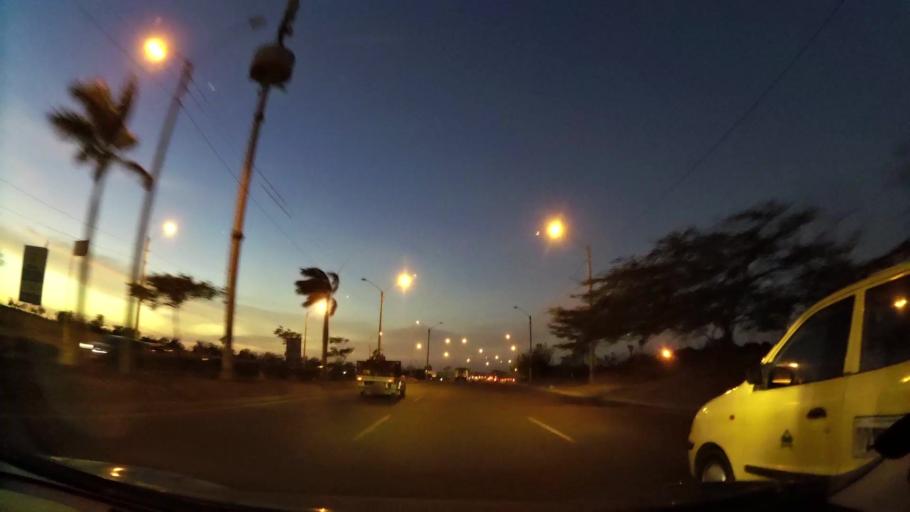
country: CO
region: Atlantico
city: Galapa
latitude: 10.9308
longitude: -74.8324
